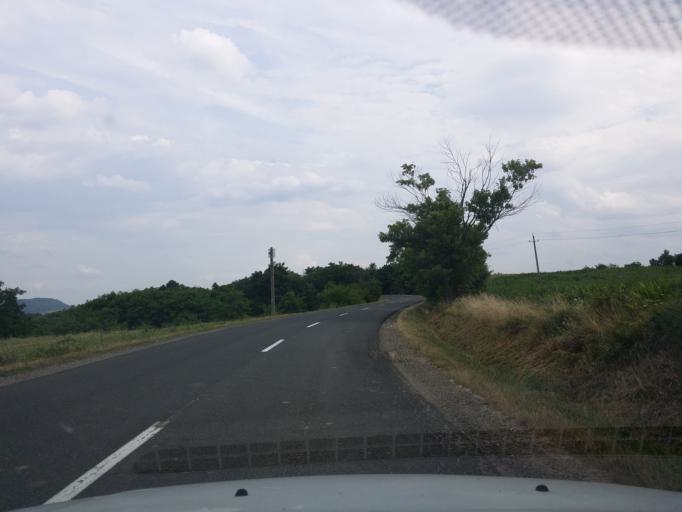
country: HU
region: Nograd
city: Bercel
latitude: 47.9248
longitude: 19.3634
